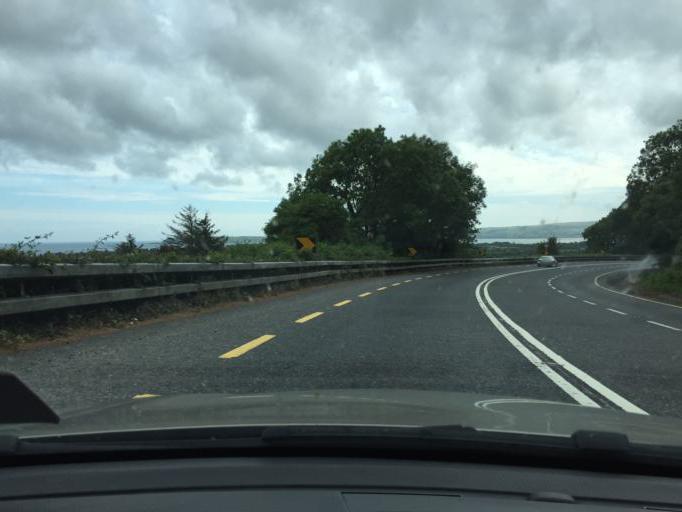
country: IE
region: Munster
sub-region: Waterford
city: Dungarvan
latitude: 52.1156
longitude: -7.5567
